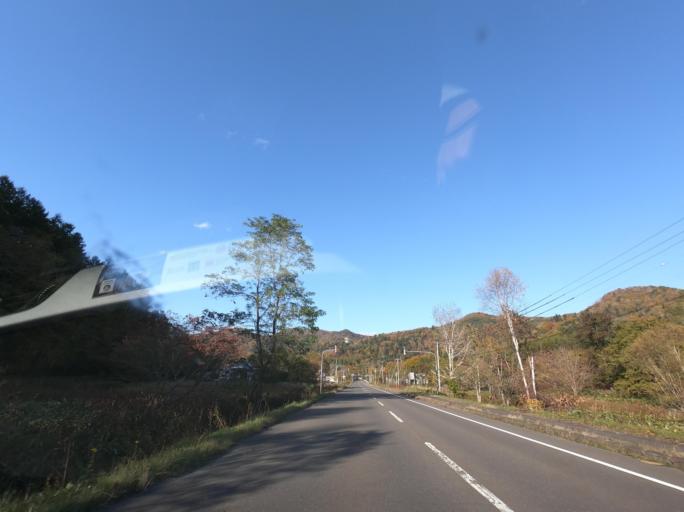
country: JP
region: Hokkaido
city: Iwamizawa
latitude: 43.0023
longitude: 142.0048
